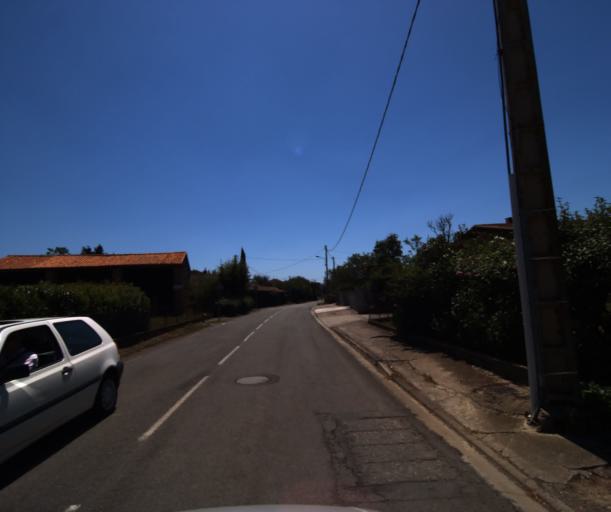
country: FR
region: Midi-Pyrenees
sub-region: Departement de la Haute-Garonne
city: Le Fauga
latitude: 43.4407
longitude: 1.2904
